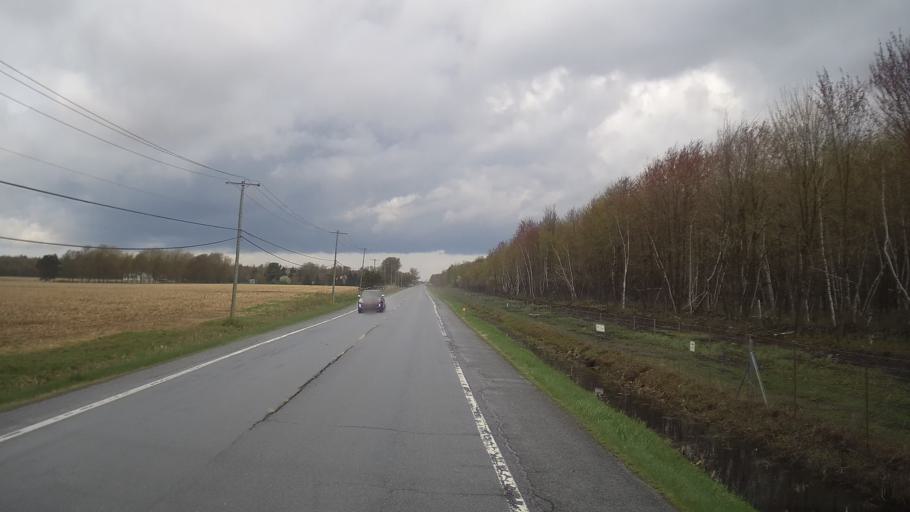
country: CA
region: Quebec
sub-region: Monteregie
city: Farnham
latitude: 45.2964
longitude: -73.0264
